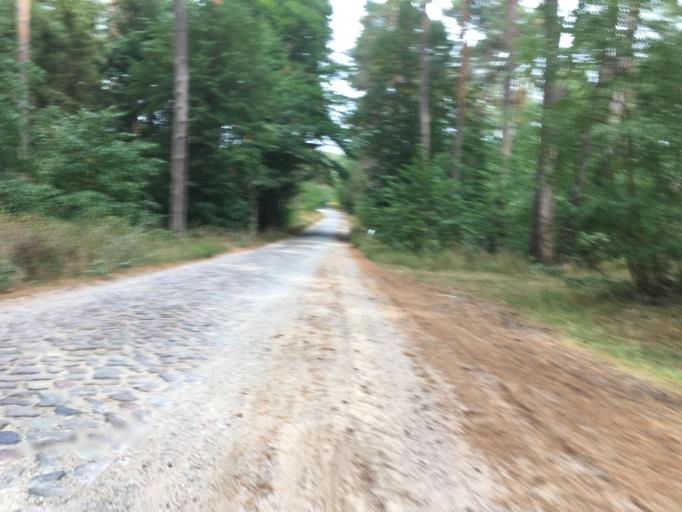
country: DE
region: Brandenburg
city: Milmersdorf
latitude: 53.0584
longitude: 13.6249
